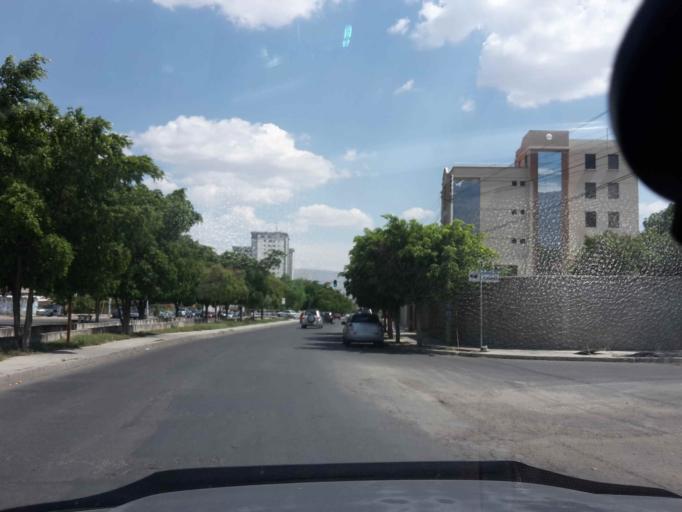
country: BO
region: Cochabamba
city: Cochabamba
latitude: -17.3681
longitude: -66.1797
